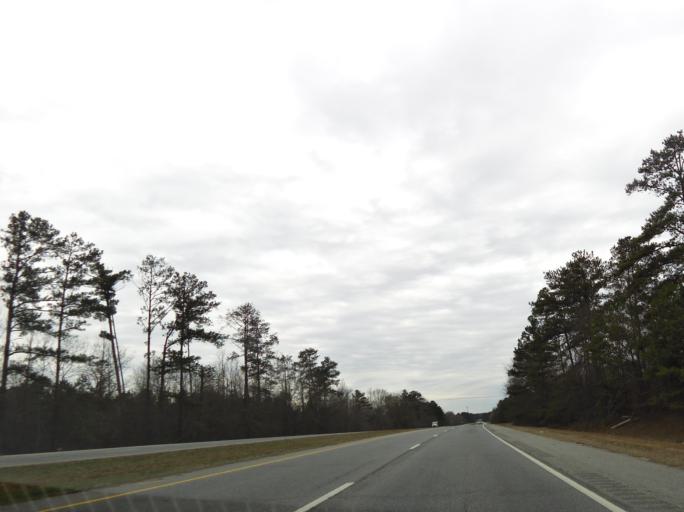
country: US
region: Georgia
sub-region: Bibb County
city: West Point
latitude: 32.8009
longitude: -83.7433
